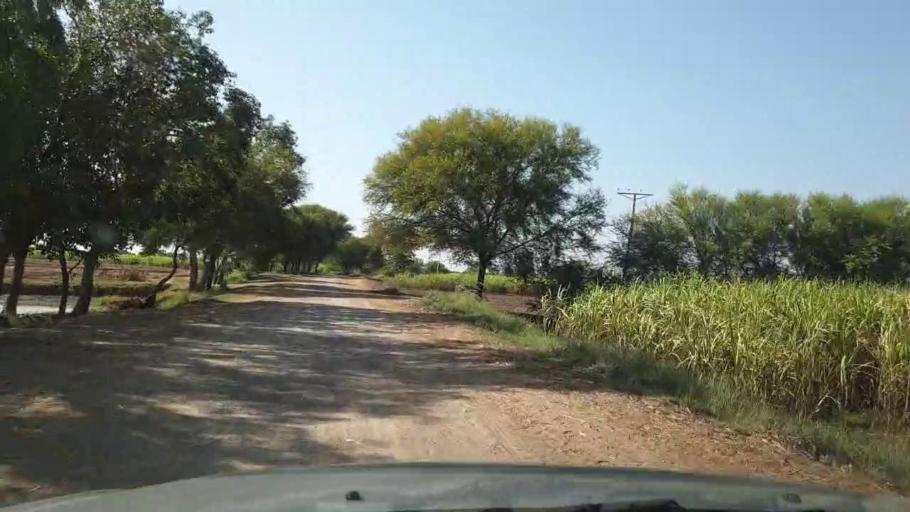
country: PK
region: Sindh
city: Bulri
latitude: 24.9528
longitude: 68.3202
